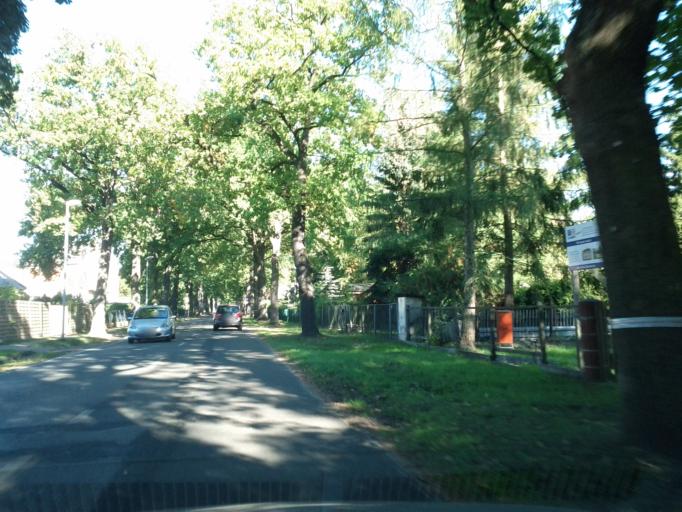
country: DE
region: Brandenburg
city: Schoneiche
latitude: 52.4675
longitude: 13.6955
